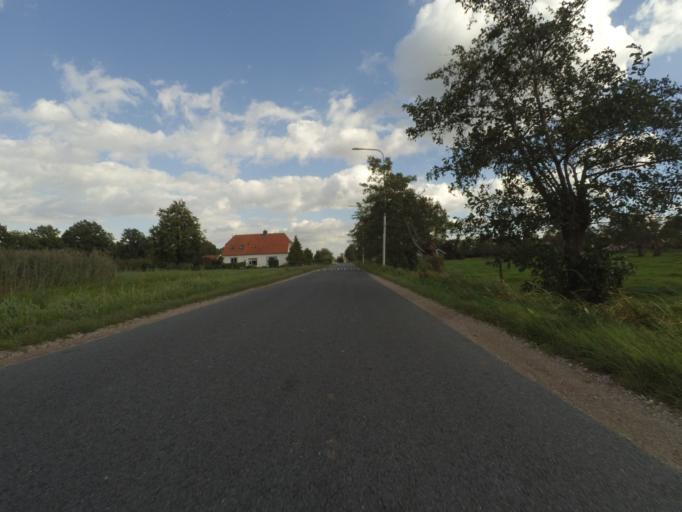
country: NL
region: Gelderland
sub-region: Gemeente Ede
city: Ederveen
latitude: 52.0569
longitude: 5.5855
